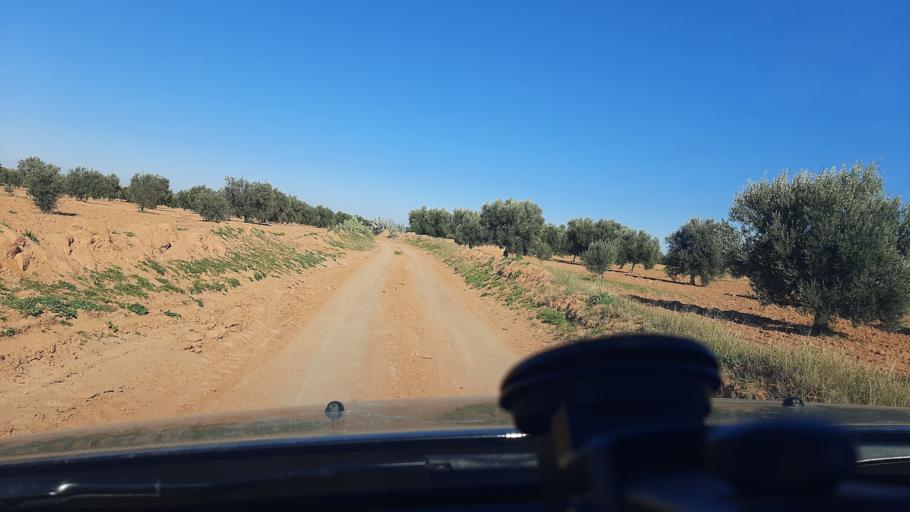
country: TN
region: Safaqis
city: Bi'r `Ali Bin Khalifah
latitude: 35.0018
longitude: 10.0861
